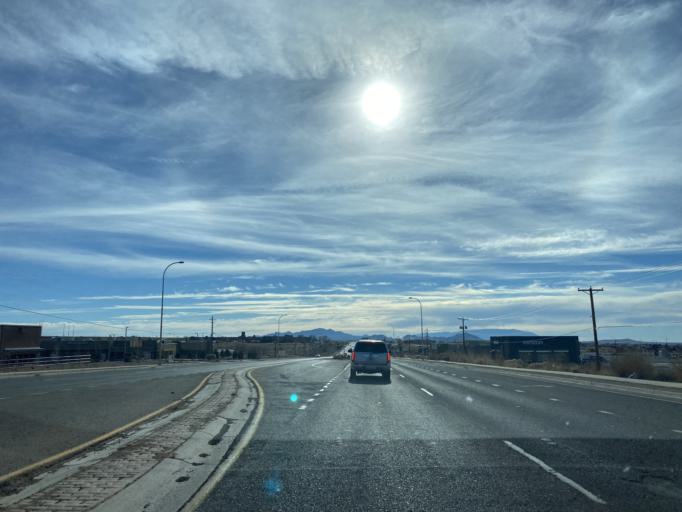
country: US
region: New Mexico
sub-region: Santa Fe County
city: Agua Fria
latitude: 35.6197
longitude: -106.0293
